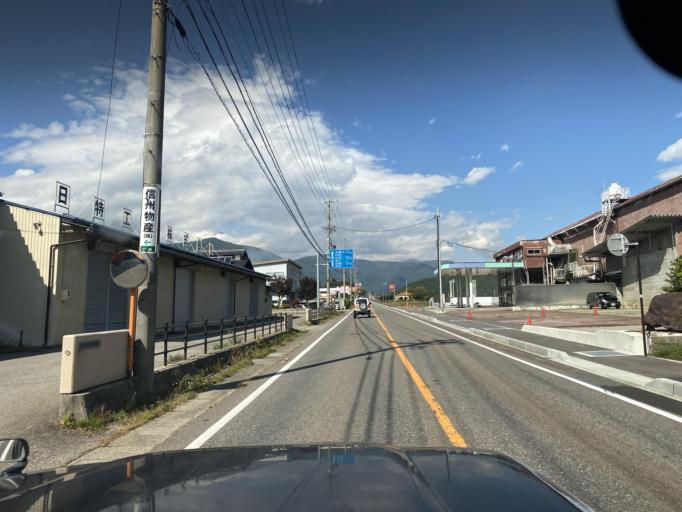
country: JP
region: Nagano
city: Omachi
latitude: 36.5280
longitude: 137.8493
